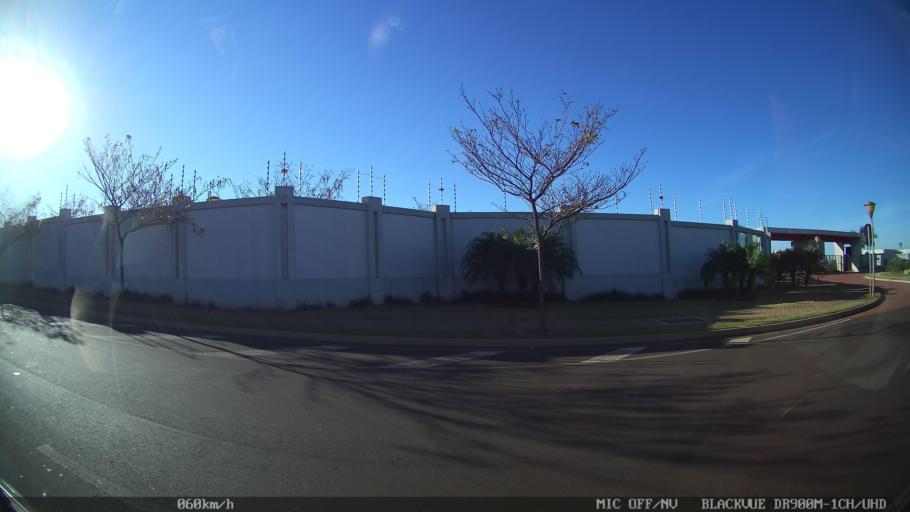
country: BR
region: Sao Paulo
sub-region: Franca
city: Franca
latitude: -20.5747
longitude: -47.4089
